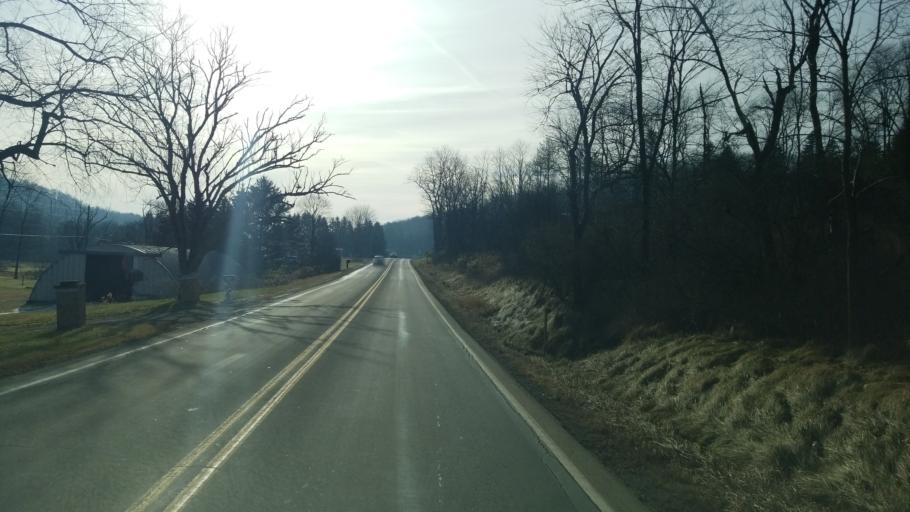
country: US
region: Pennsylvania
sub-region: Indiana County
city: Chevy Chase Heights
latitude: 40.7773
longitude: -79.1547
